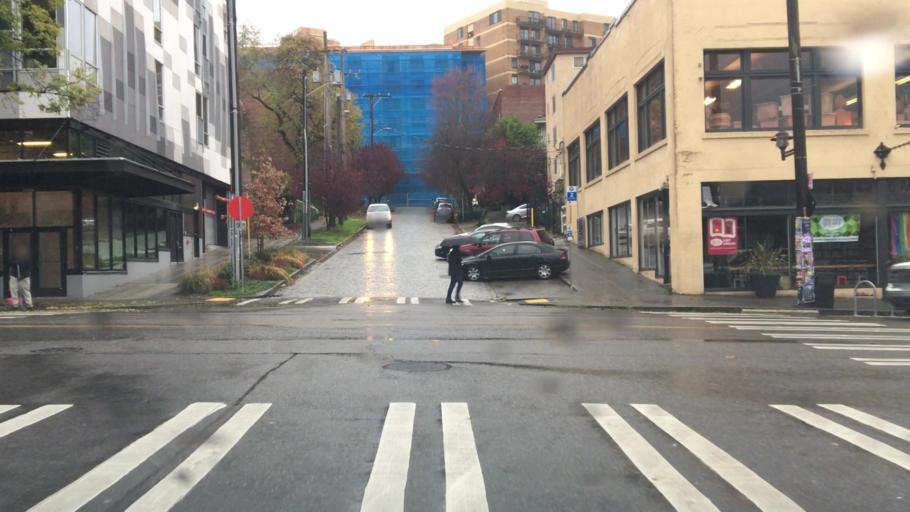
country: US
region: Washington
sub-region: King County
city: Seattle
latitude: 47.6143
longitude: -122.3244
